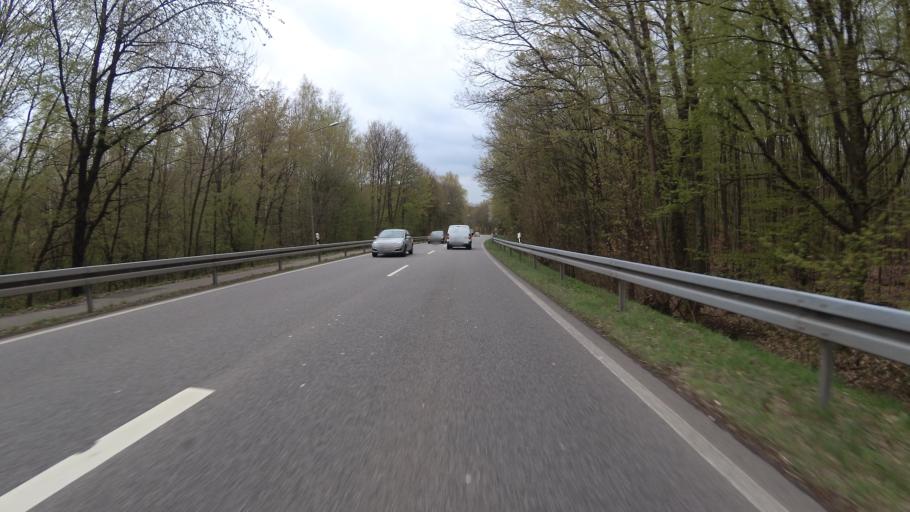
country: DE
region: Saarland
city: Friedrichsthal
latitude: 49.3374
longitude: 7.0786
